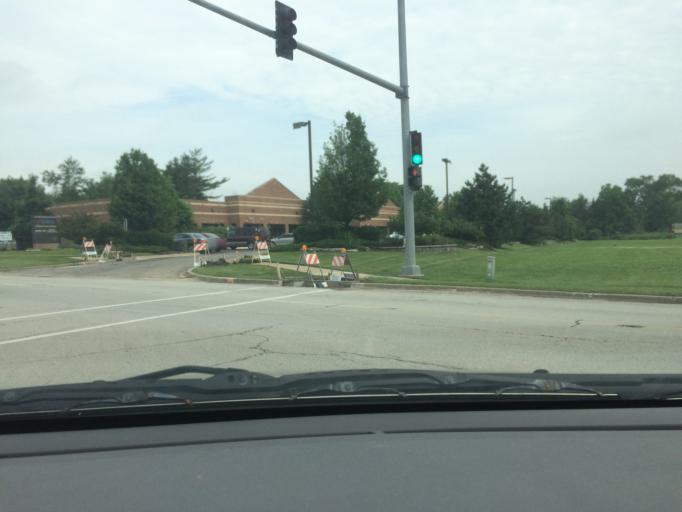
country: US
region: Illinois
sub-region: DuPage County
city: Carol Stream
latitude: 41.9428
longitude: -88.1730
